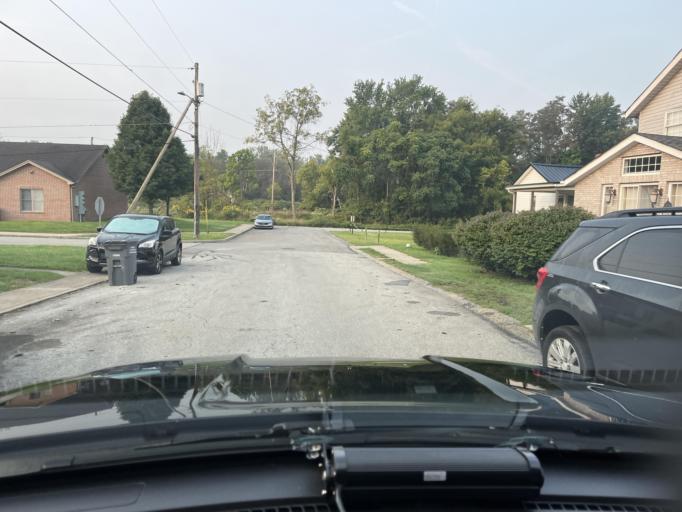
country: US
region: Pennsylvania
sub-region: Fayette County
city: Uniontown
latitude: 39.8929
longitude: -79.7173
